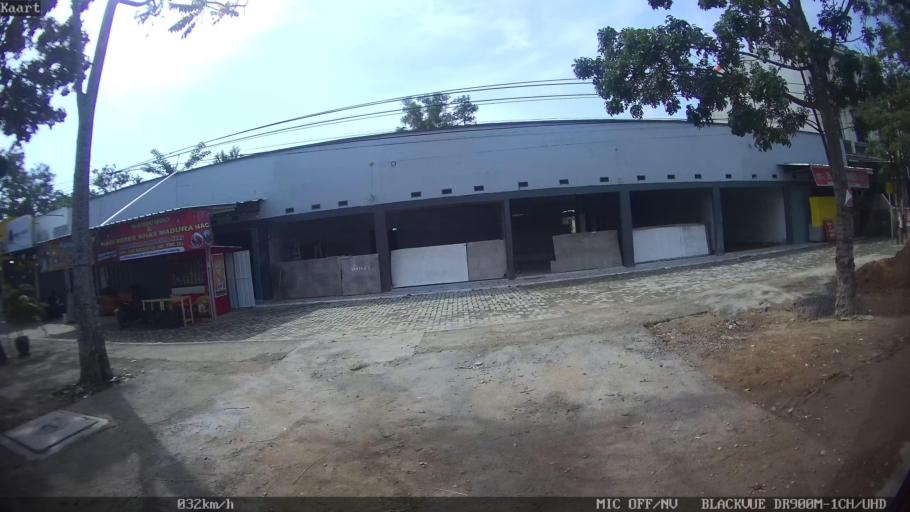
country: ID
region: Lampung
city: Kedaton
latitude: -5.3825
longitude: 105.2980
